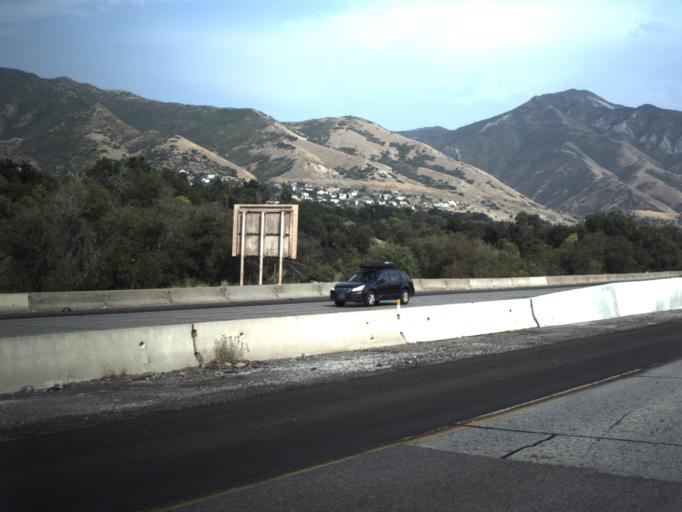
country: US
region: Utah
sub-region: Salt Lake County
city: Willard
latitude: 40.7160
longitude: -111.8331
